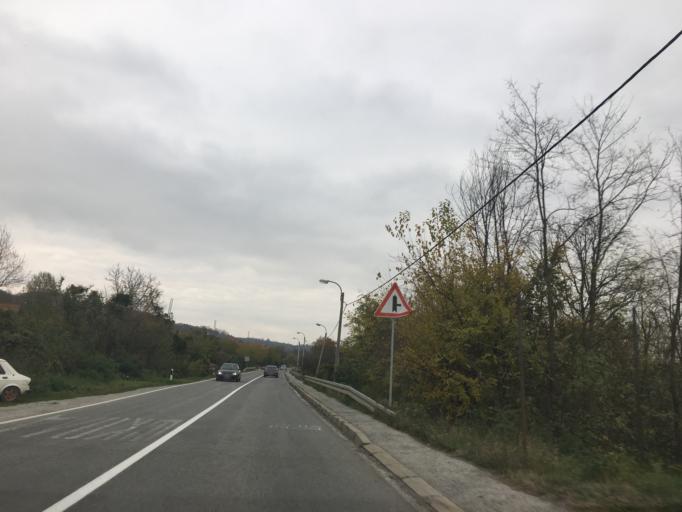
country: RS
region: Central Serbia
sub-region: Raski Okrug
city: Kraljevo
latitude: 43.7260
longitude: 20.7610
